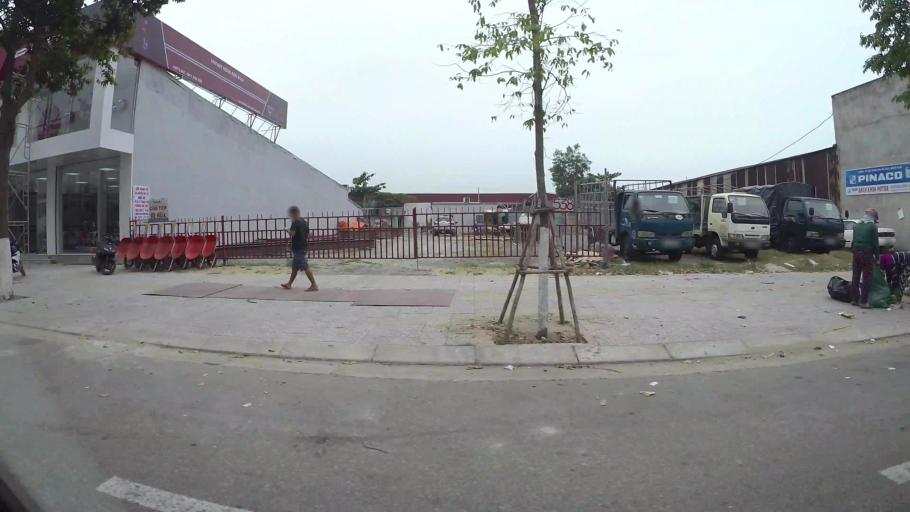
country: VN
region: Da Nang
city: Cam Le
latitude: 16.0280
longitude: 108.2086
